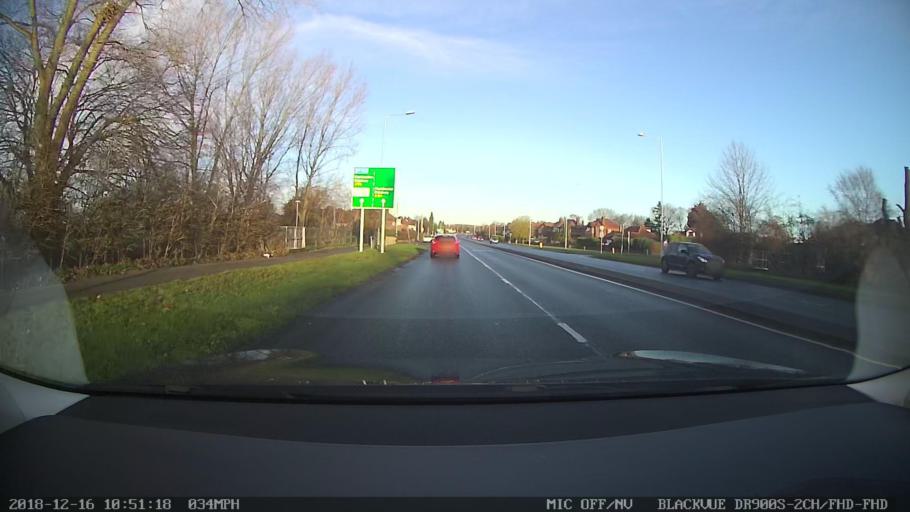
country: GB
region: England
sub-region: Manchester
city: Didsbury
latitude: 53.3871
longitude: -2.2245
